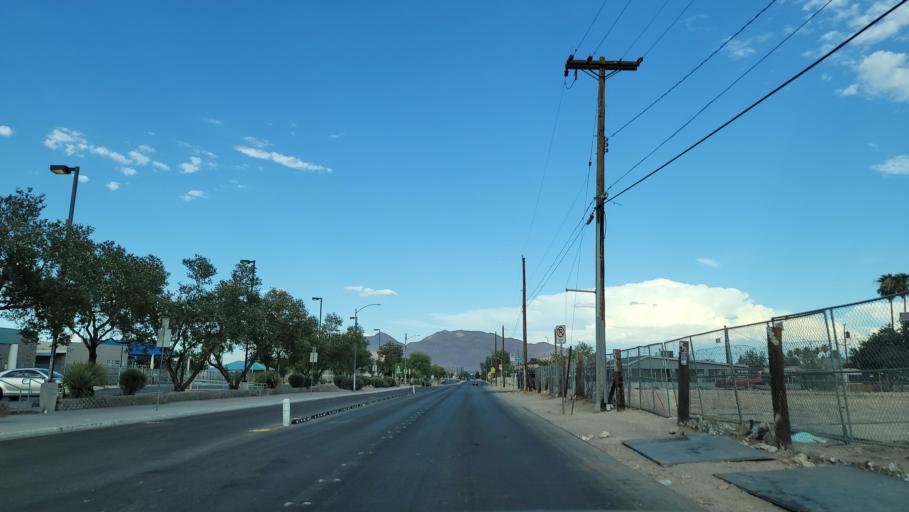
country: US
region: Nevada
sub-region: Clark County
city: North Las Vegas
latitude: 36.1775
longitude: -115.1137
